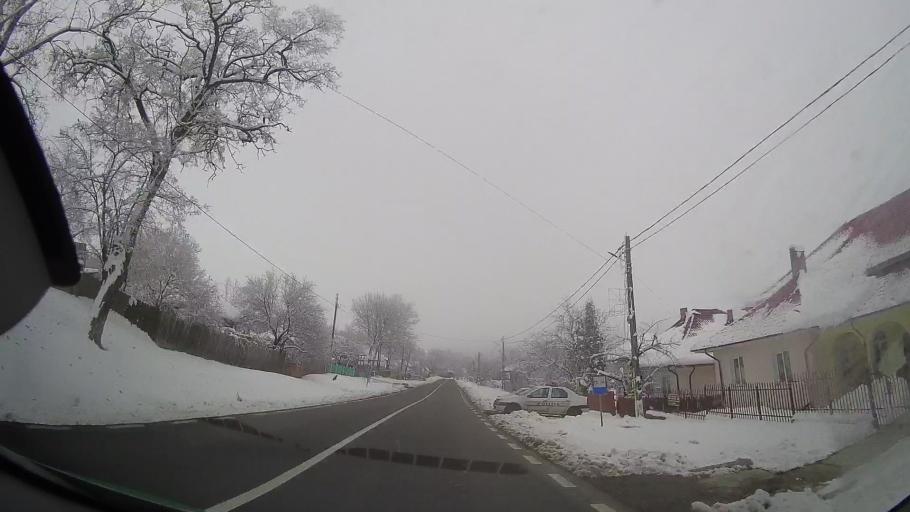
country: RO
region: Neamt
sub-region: Comuna Poenari
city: Poienari
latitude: 46.8856
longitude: 27.1312
